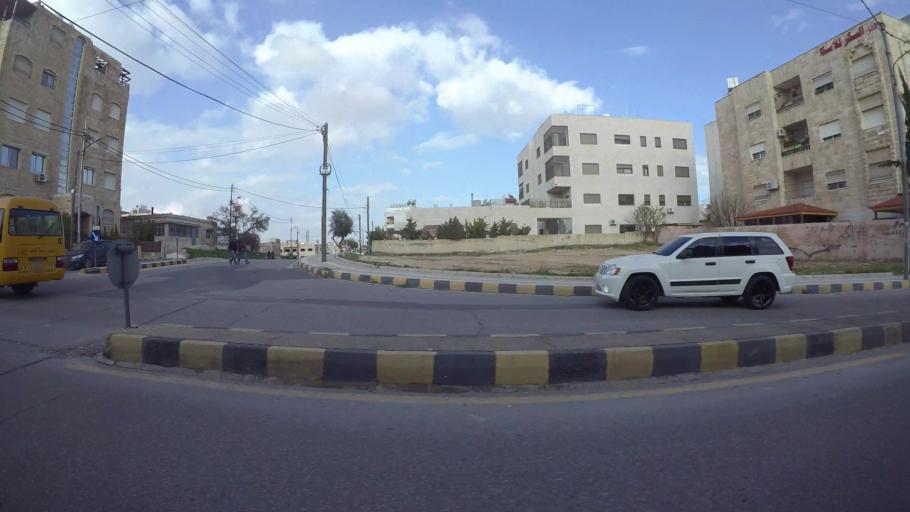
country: JO
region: Amman
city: Al Jubayhah
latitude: 31.9879
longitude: 35.8555
